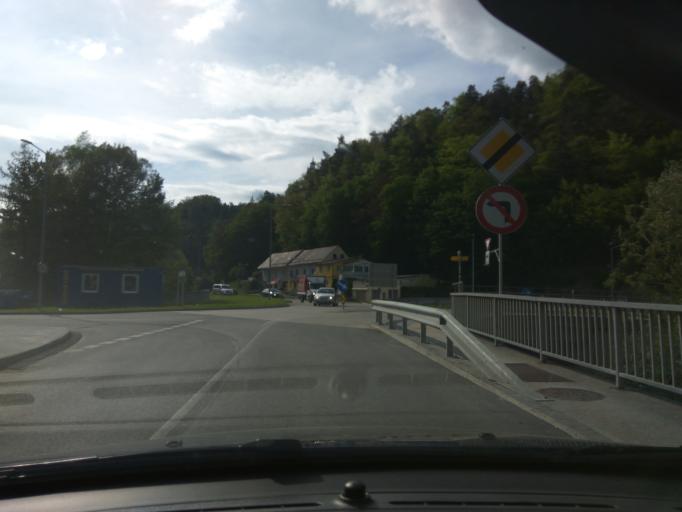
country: AT
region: Styria
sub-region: Politischer Bezirk Voitsberg
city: Ligist
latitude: 47.0223
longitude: 15.1975
